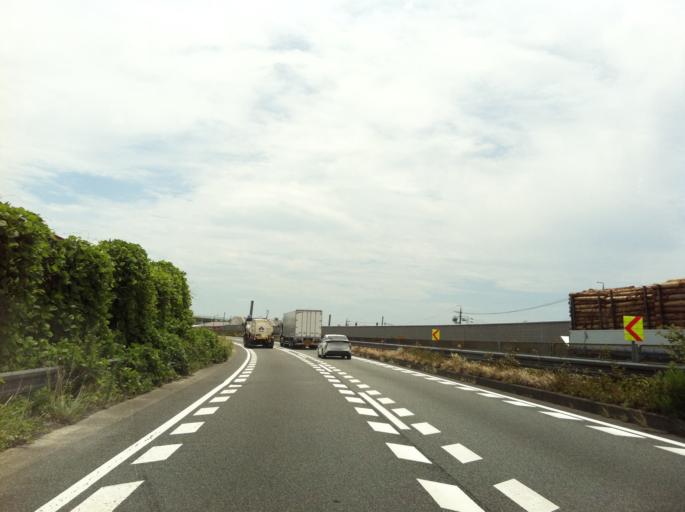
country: JP
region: Shizuoka
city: Fuji
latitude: 35.1235
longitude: 138.6232
